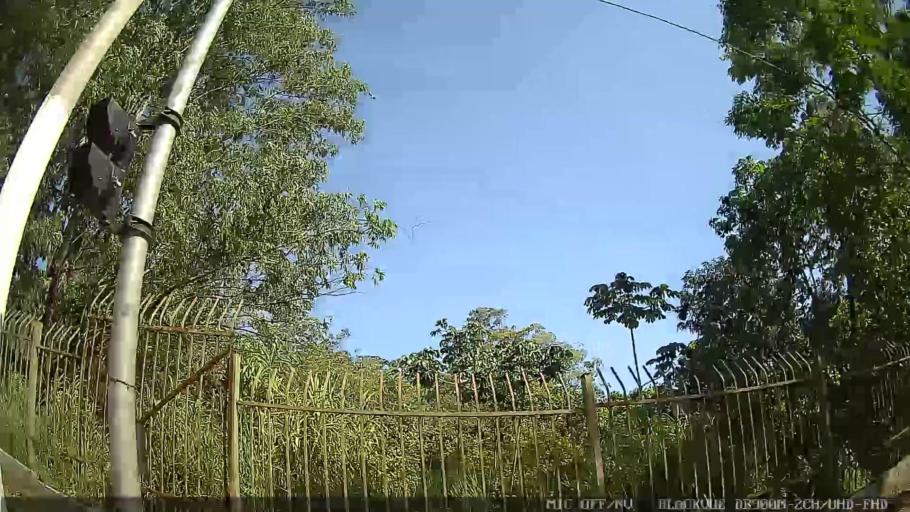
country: BR
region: Sao Paulo
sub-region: Sao Caetano Do Sul
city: Sao Caetano do Sul
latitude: -23.5759
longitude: -46.4788
